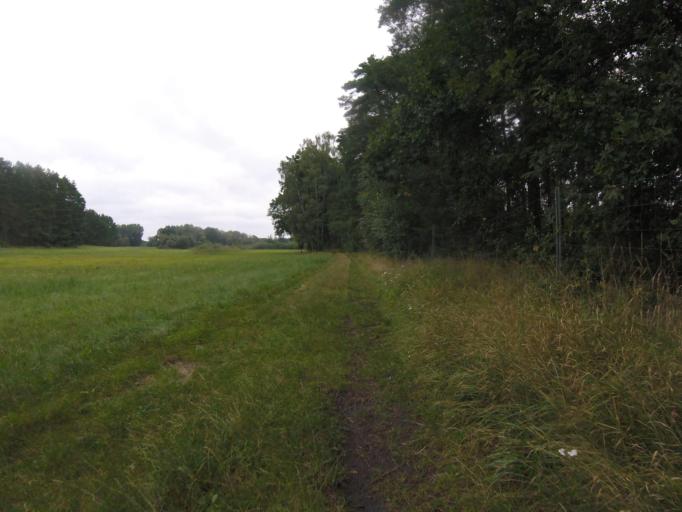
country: DE
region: Brandenburg
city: Bestensee
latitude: 52.2162
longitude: 13.6453
